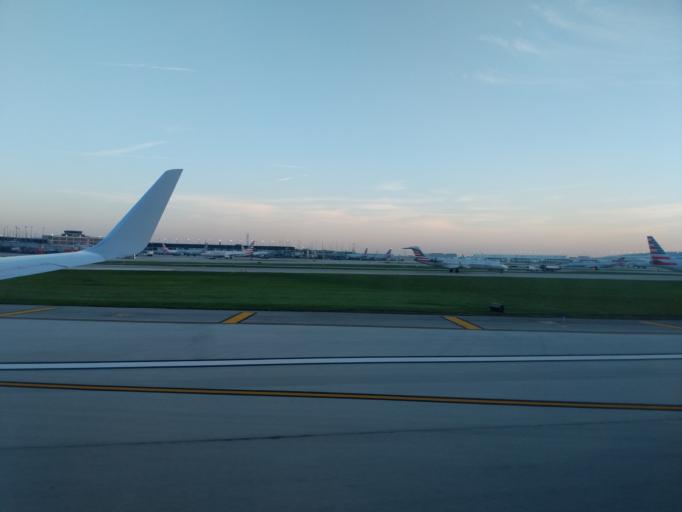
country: US
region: Illinois
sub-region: Cook County
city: Rosemont
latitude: 41.9690
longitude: -87.8981
